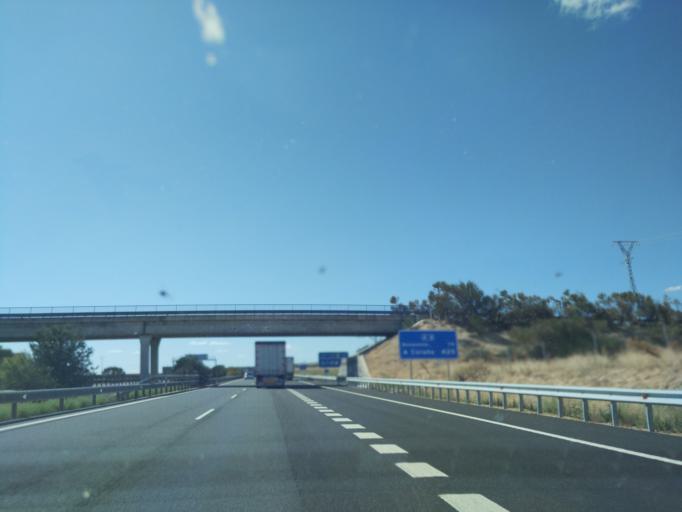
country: ES
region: Castille and Leon
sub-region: Provincia de Valladolid
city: Tordesillas
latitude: 41.5167
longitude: -5.0282
